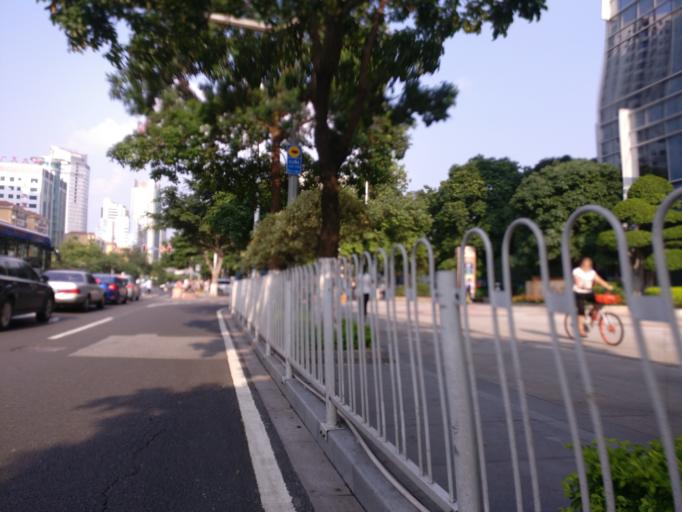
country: CN
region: Guangdong
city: Wushan
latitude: 23.1297
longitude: 113.3219
